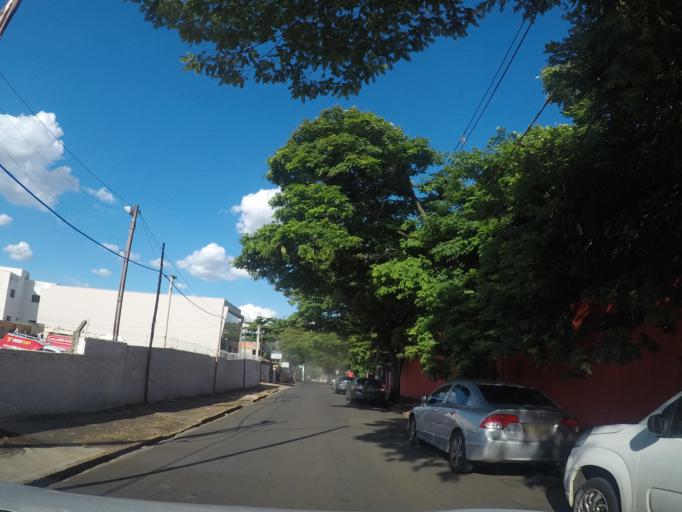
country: BR
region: Sao Paulo
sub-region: Sumare
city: Sumare
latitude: -22.8253
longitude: -47.2672
